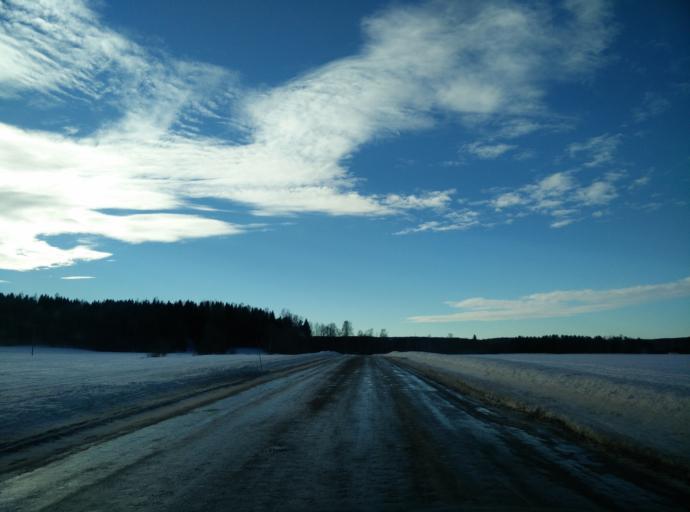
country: SE
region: Vaesternorrland
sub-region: Sundsvalls Kommun
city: Skottsund
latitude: 62.2791
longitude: 17.4008
